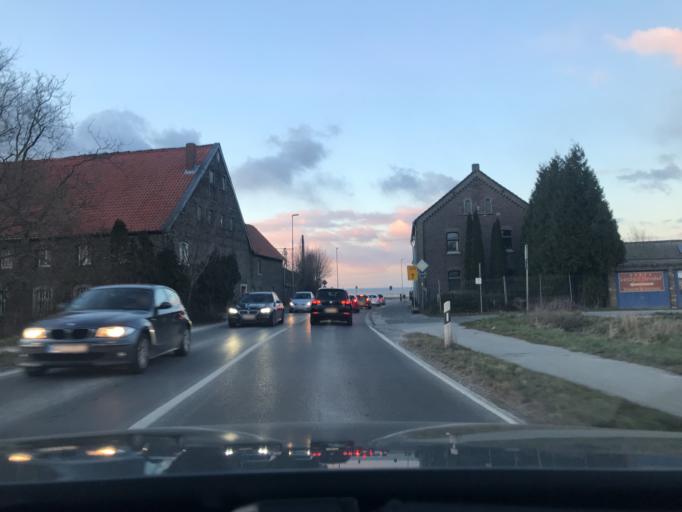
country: DE
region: North Rhine-Westphalia
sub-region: Regierungsbezirk Dusseldorf
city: Kaarst
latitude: 51.2490
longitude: 6.6191
